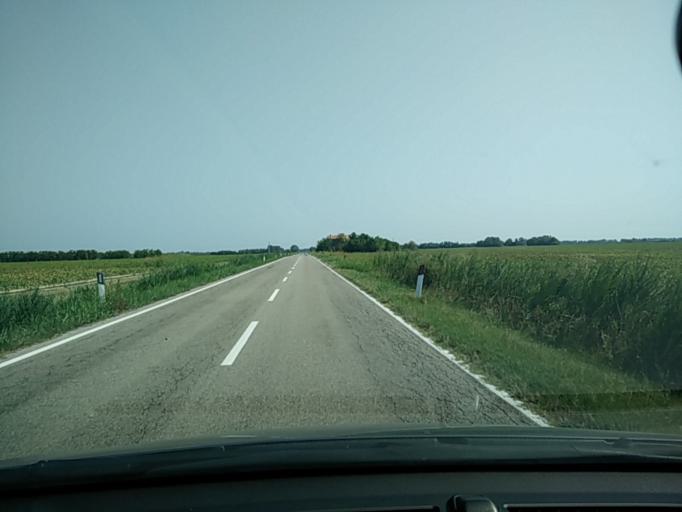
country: IT
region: Veneto
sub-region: Provincia di Venezia
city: La Salute di Livenza
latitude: 45.6391
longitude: 12.8286
